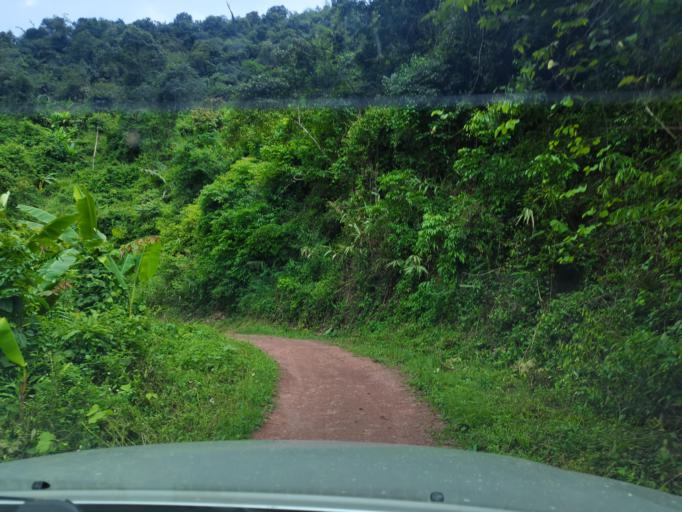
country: LA
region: Loungnamtha
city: Muang Nale
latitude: 20.5154
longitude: 101.0761
